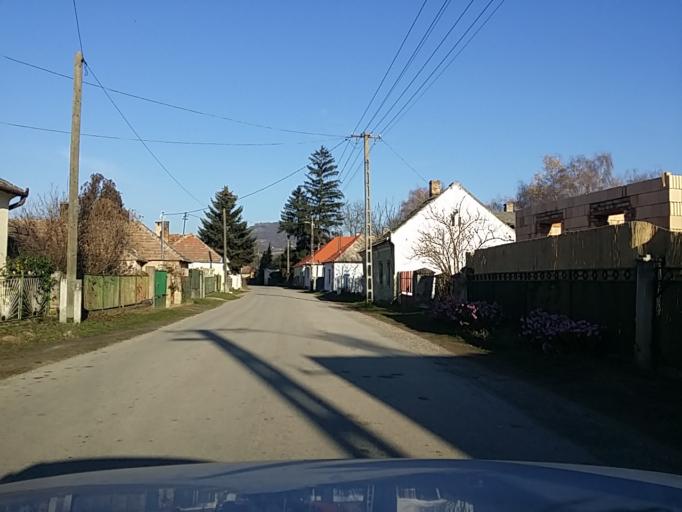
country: HU
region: Veszprem
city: Badacsonytomaj
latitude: 46.8462
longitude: 17.5144
